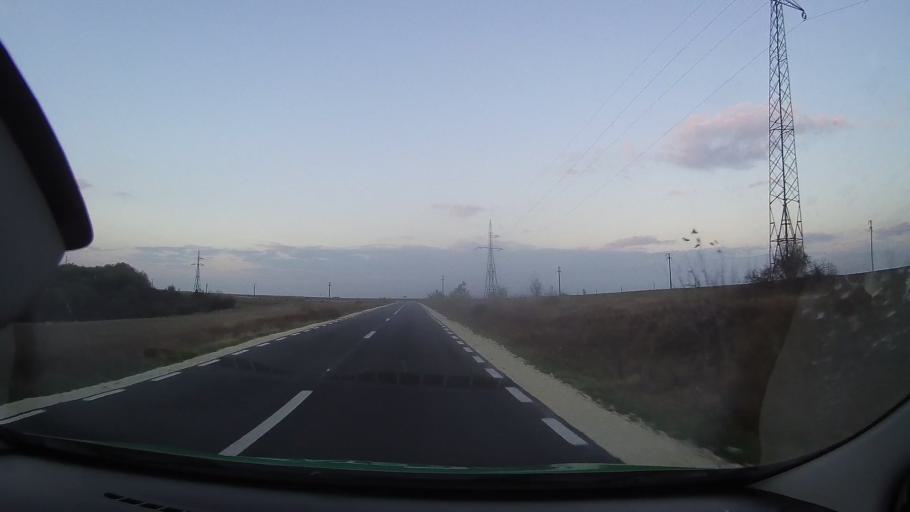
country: RO
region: Constanta
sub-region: Comuna Baneasa
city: Baneasa
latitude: 44.0913
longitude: 27.6872
